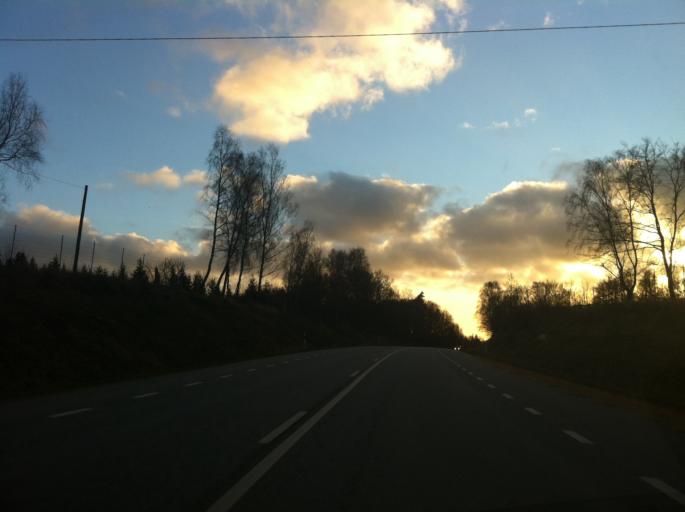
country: SE
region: Skane
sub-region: Hassleholms Kommun
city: Sosdala
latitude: 56.0007
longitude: 13.6427
